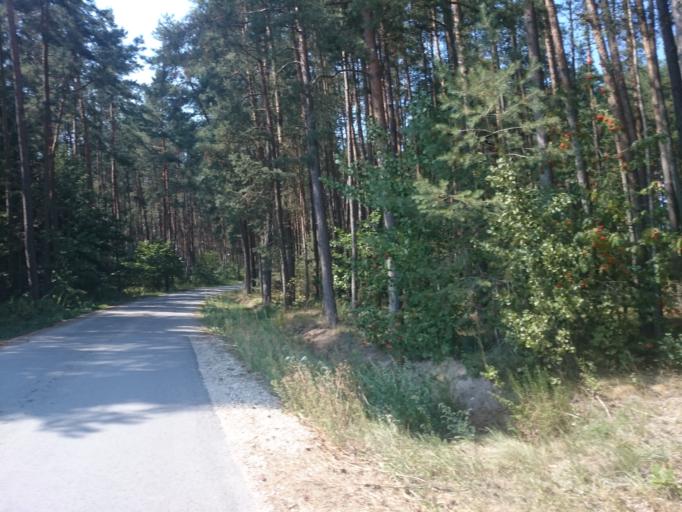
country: DE
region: Bavaria
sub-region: Regierungsbezirk Mittelfranken
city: Hilpoltstein
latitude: 49.1671
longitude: 11.1644
